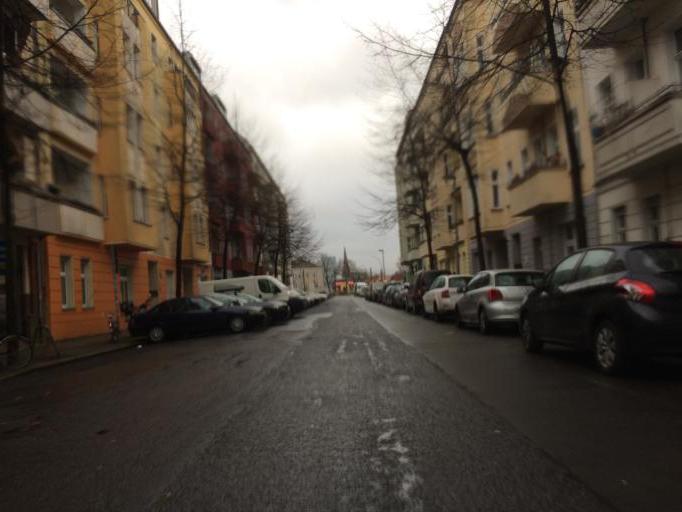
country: DE
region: Berlin
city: Friedrichshain Bezirk
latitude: 52.5103
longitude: 13.4498
